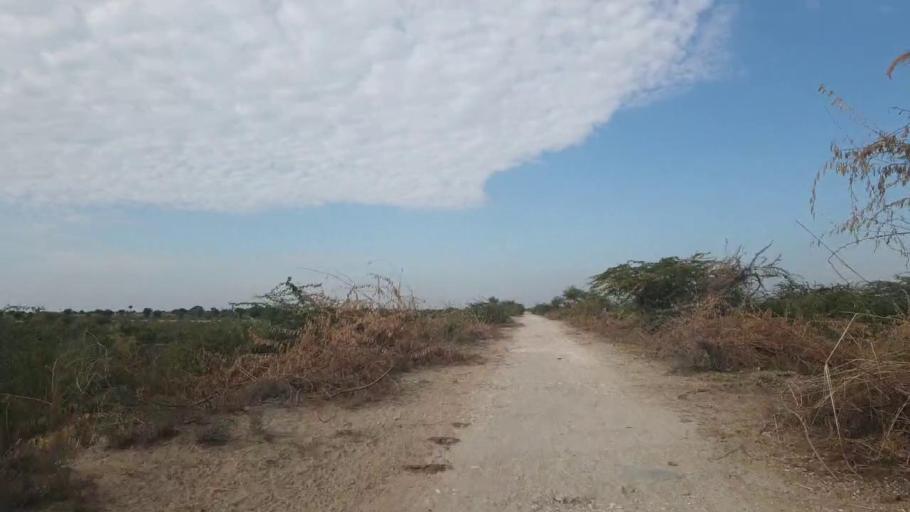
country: PK
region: Sindh
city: Sinjhoro
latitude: 26.0539
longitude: 68.8749
